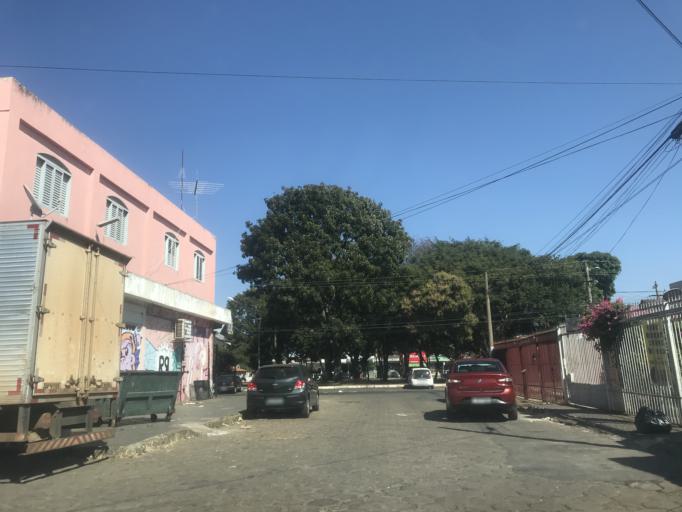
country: BR
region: Federal District
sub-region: Brasilia
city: Brasilia
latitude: -15.8175
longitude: -47.9875
